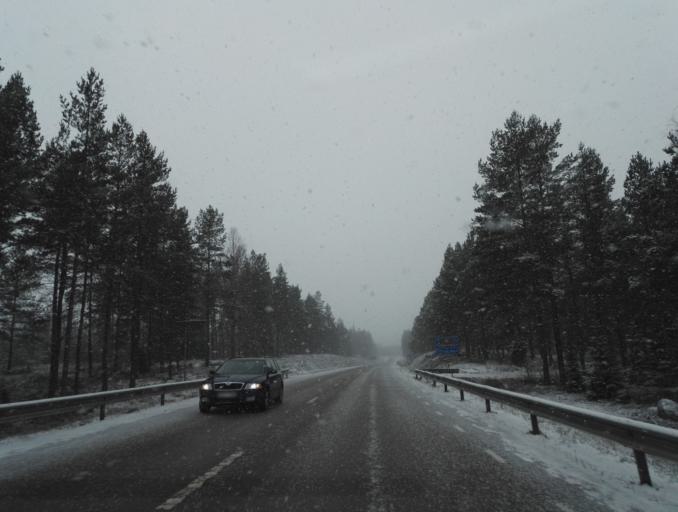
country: SE
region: Kronoberg
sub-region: Uppvidinge Kommun
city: Lenhovda
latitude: 57.0940
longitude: 15.1971
